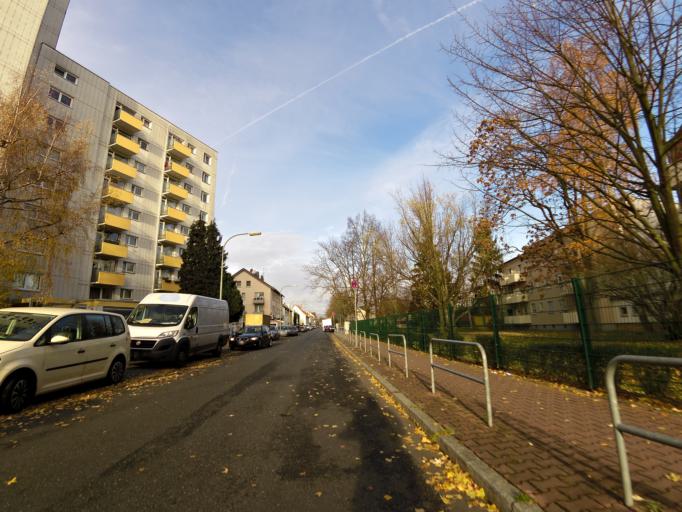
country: DE
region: Hesse
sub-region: Regierungsbezirk Darmstadt
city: Eschborn
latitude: 50.0996
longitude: 8.5731
